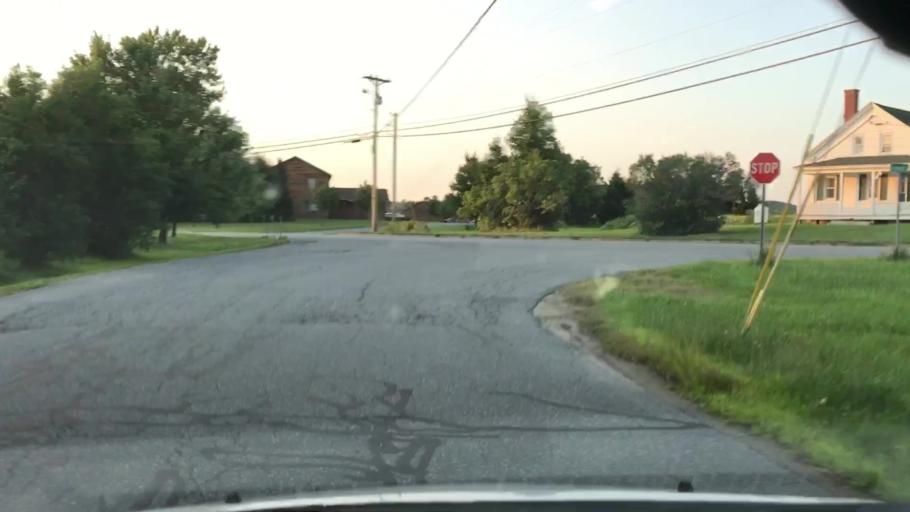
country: US
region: New Hampshire
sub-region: Grafton County
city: North Haverhill
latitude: 44.0866
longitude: -72.0195
